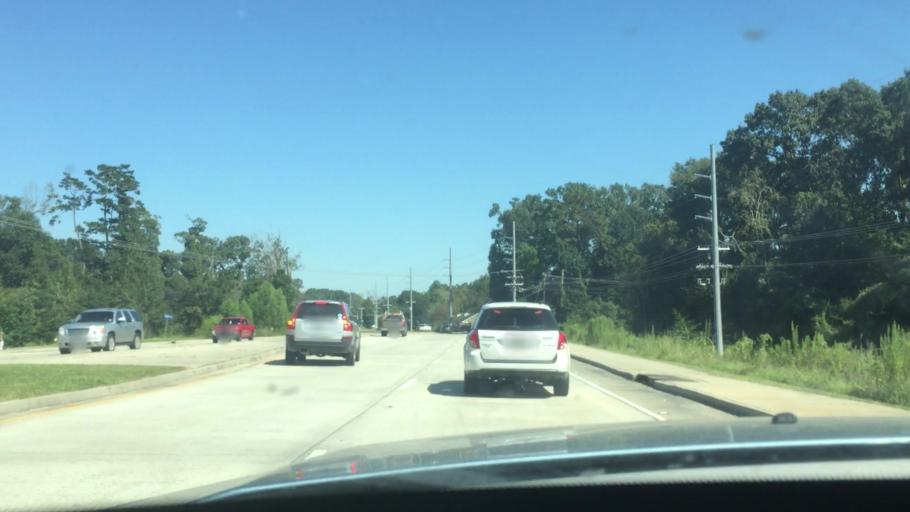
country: US
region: Louisiana
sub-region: East Baton Rouge Parish
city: Shenandoah
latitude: 30.4262
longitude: -91.0118
